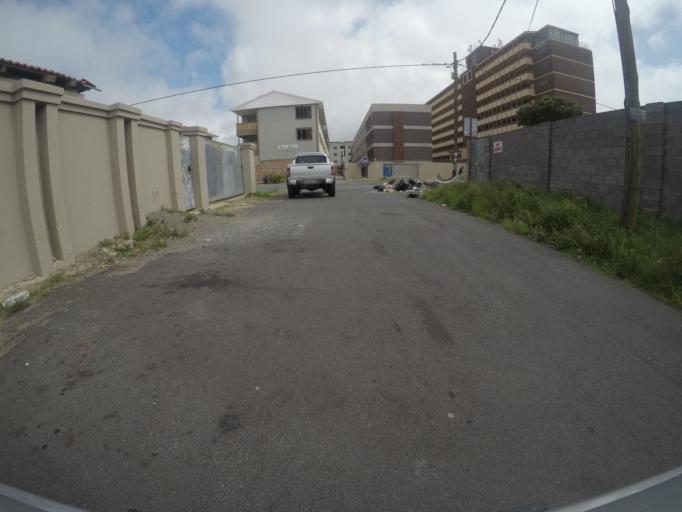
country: ZA
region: Eastern Cape
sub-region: Buffalo City Metropolitan Municipality
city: East London
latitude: -32.9996
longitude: 27.9058
